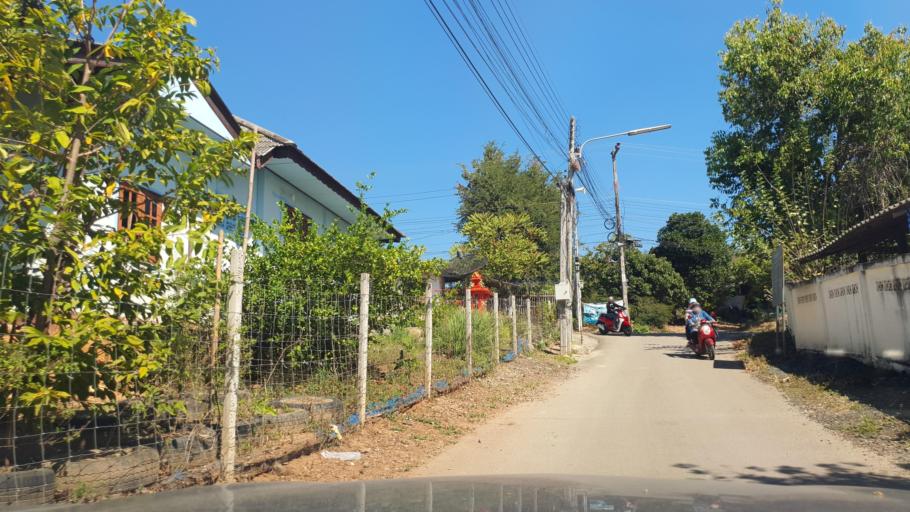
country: TH
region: Chiang Mai
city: Mae Wang
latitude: 18.6794
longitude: 98.8189
